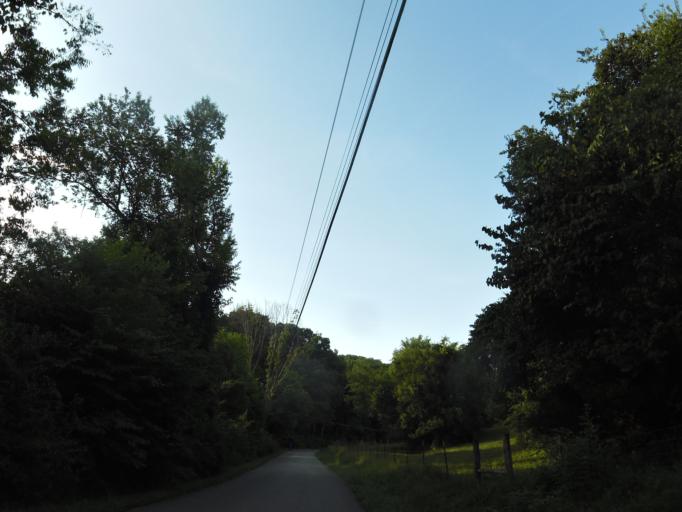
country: US
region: Tennessee
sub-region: Blount County
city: Eagleton Village
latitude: 35.8256
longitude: -83.9185
